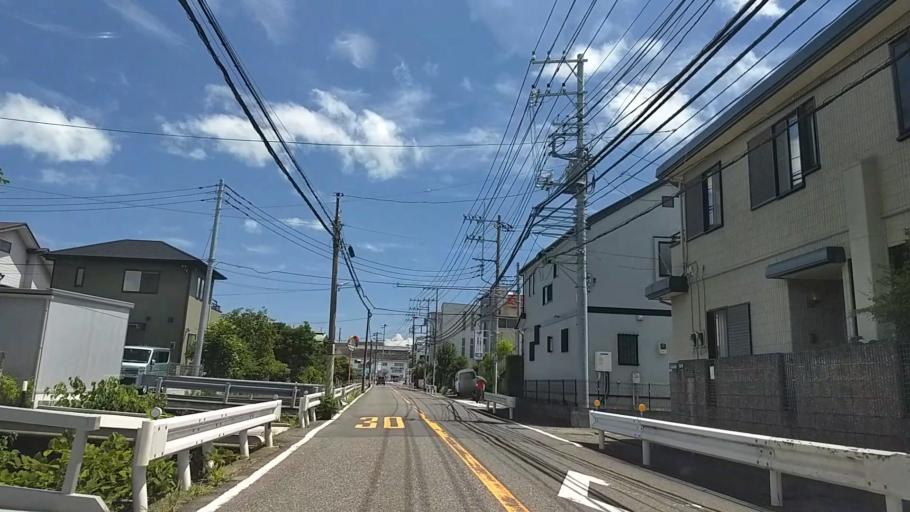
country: JP
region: Kanagawa
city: Kamakura
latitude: 35.3429
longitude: 139.5353
